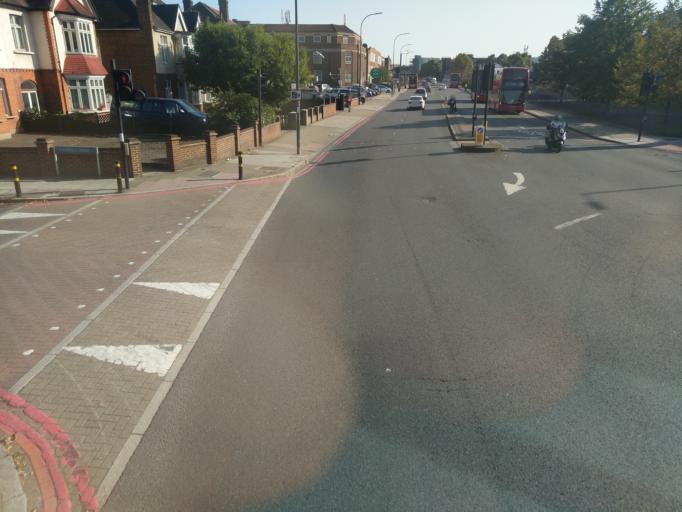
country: GB
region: England
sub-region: Greater London
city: Catford
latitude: 51.4362
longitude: -0.0181
